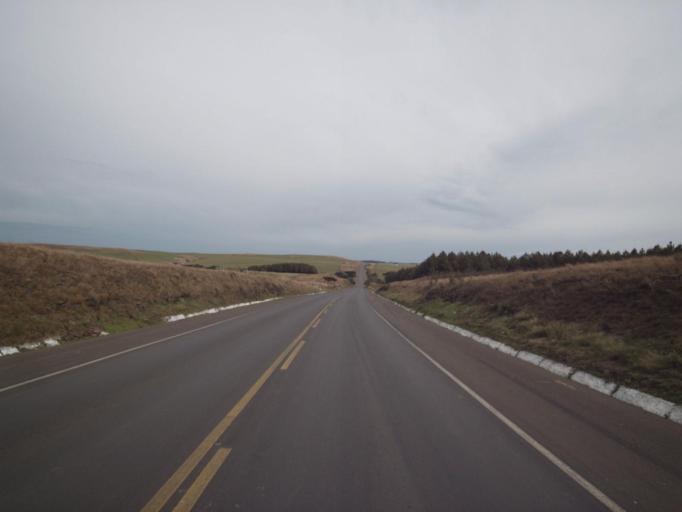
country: BR
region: Parana
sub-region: Palmas
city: Palmas
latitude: -26.7550
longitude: -51.6640
